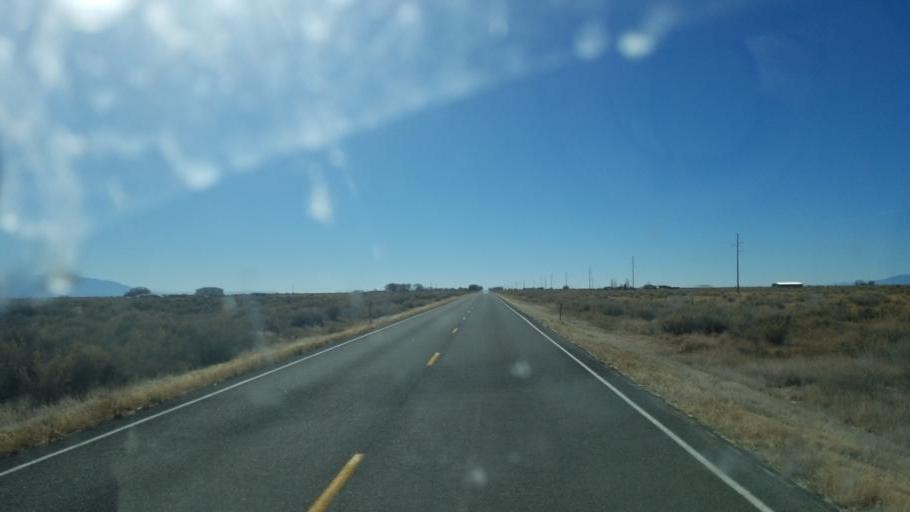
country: US
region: Colorado
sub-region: Saguache County
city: Saguache
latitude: 38.0331
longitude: -105.9123
